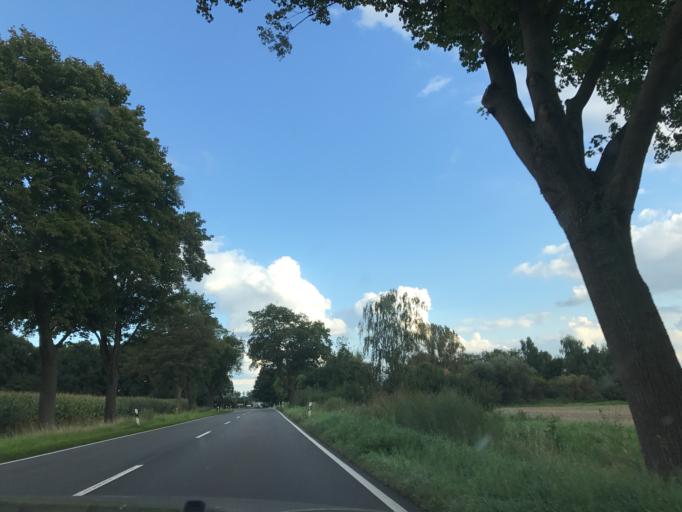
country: DE
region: Lower Saxony
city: Klein Schwulper
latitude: 52.3279
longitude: 10.4340
